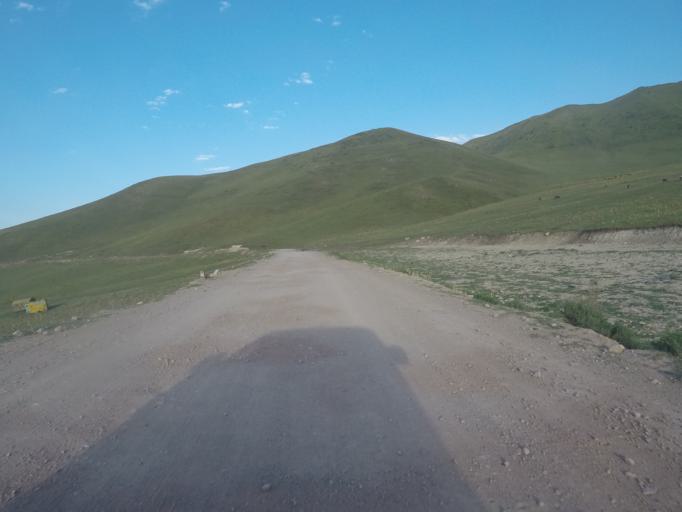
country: KG
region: Chuy
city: Bishkek
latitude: 42.6400
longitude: 74.6390
